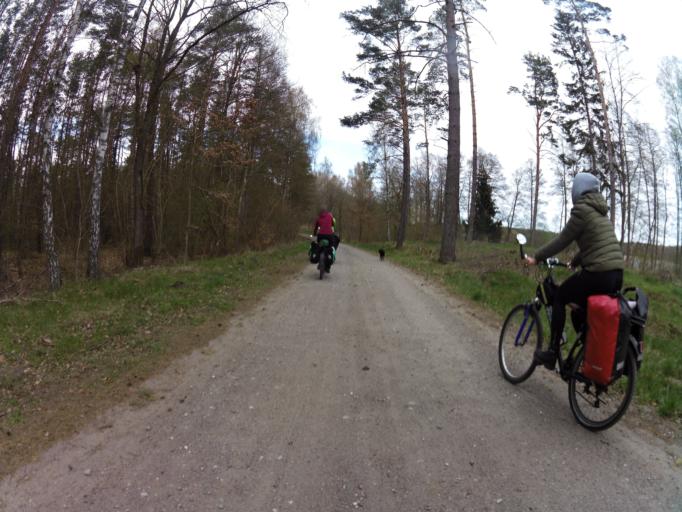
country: PL
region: West Pomeranian Voivodeship
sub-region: Powiat koszalinski
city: Bobolice
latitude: 53.8632
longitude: 16.6852
